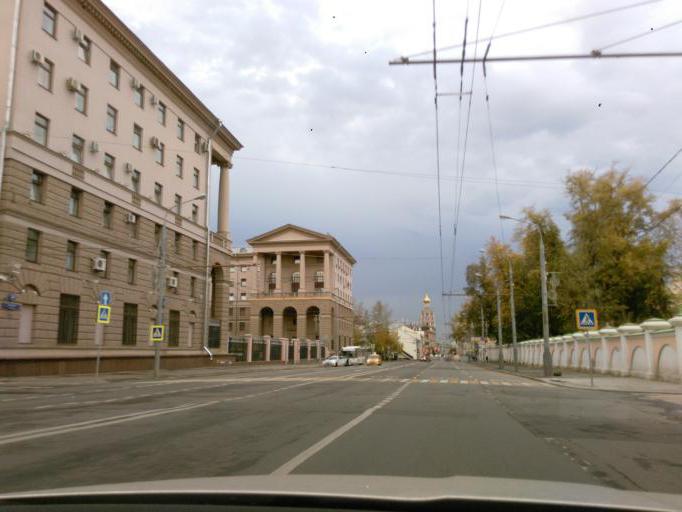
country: RU
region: Moscow
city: Moscow
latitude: 55.7704
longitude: 37.6114
